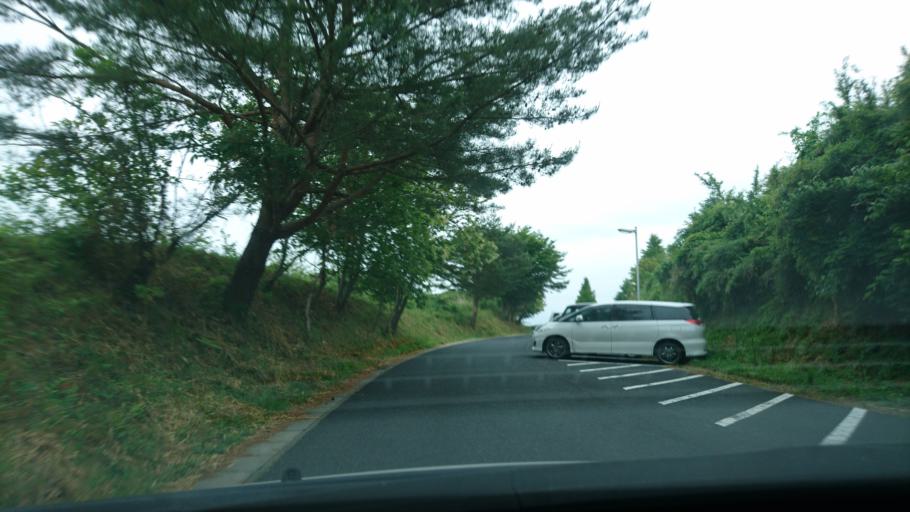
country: JP
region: Iwate
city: Ichinoseki
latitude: 38.9374
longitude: 141.1706
